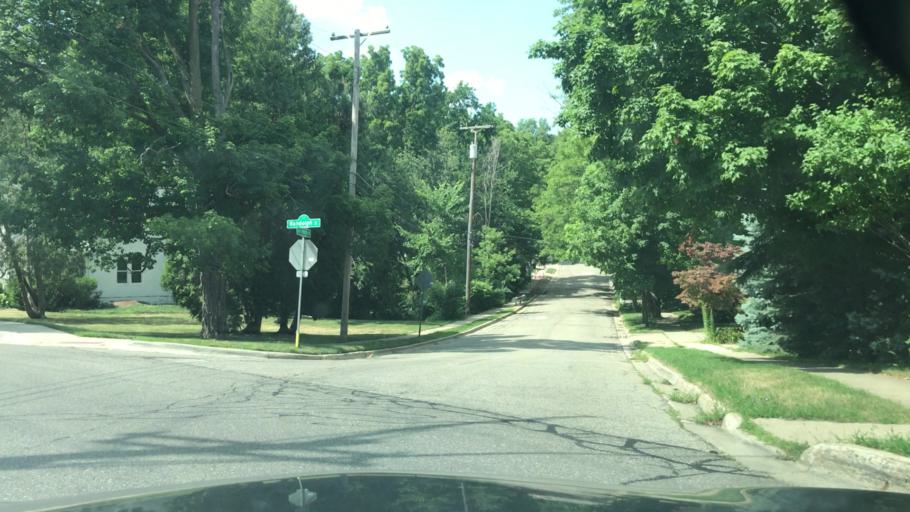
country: US
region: Michigan
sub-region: Wayne County
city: Northville
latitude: 42.4334
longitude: -83.4859
